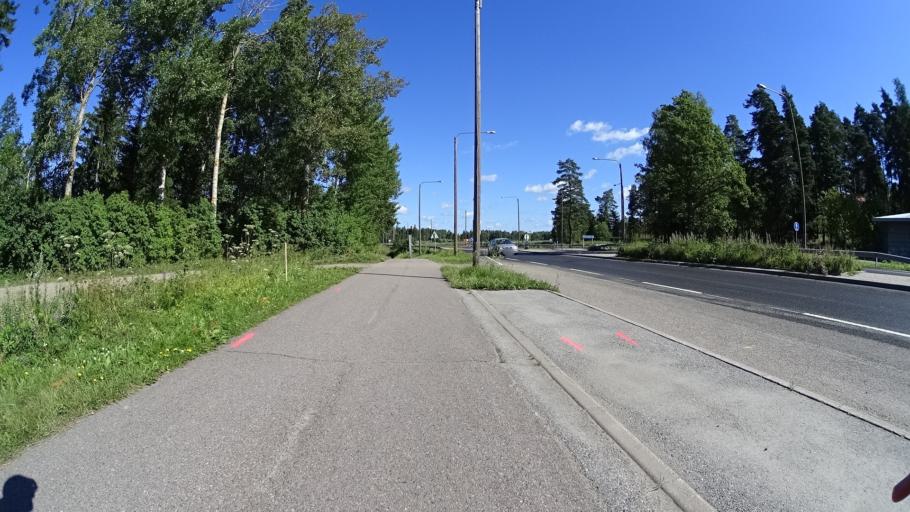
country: FI
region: Uusimaa
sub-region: Helsinki
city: Jaervenpaeae
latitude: 60.4457
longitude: 25.0776
